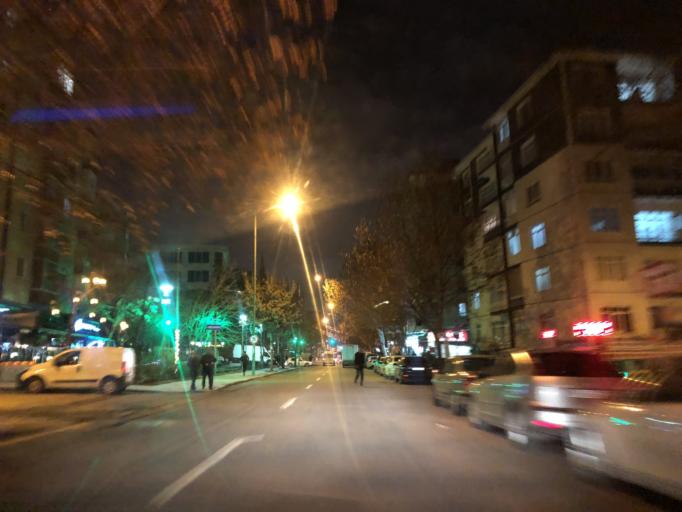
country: TR
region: Ankara
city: Batikent
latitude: 39.9669
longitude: 32.7901
